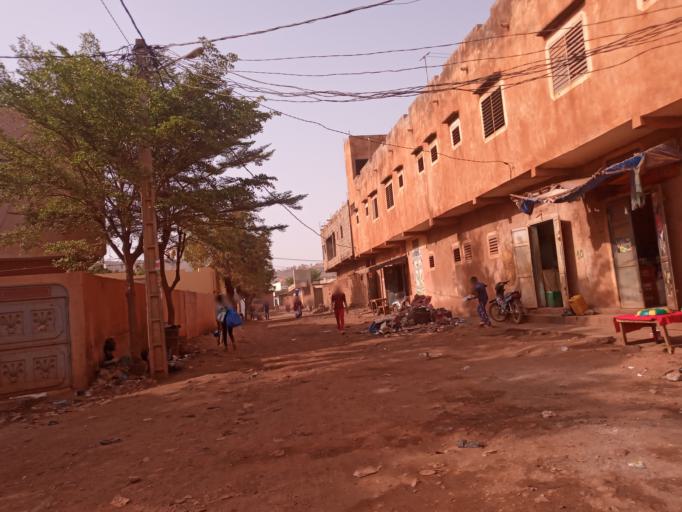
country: ML
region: Bamako
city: Bamako
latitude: 12.6822
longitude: -7.9409
